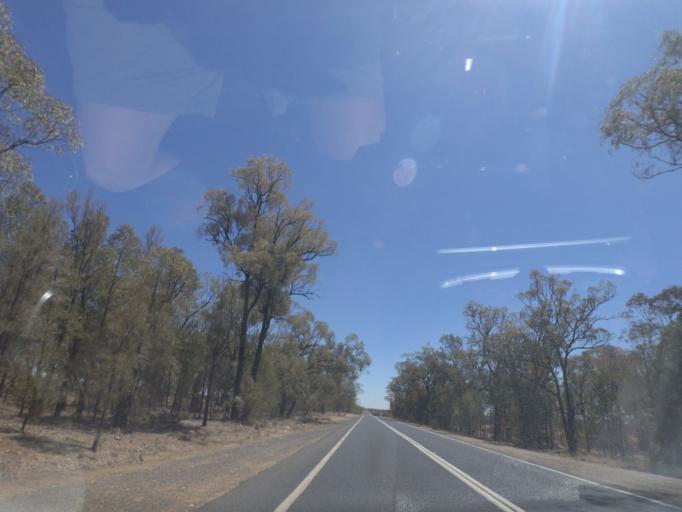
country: AU
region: New South Wales
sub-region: Gilgandra
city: Gilgandra
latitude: -31.4859
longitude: 148.8796
